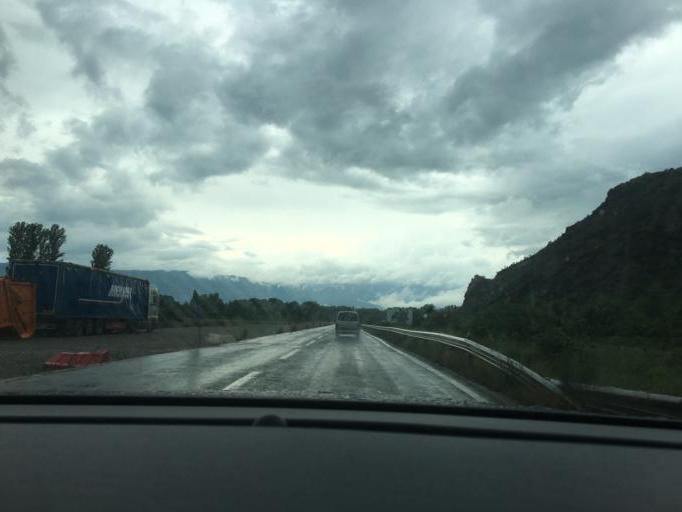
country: MK
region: Ohrid
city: Ohrid
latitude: 41.1384
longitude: 20.7671
